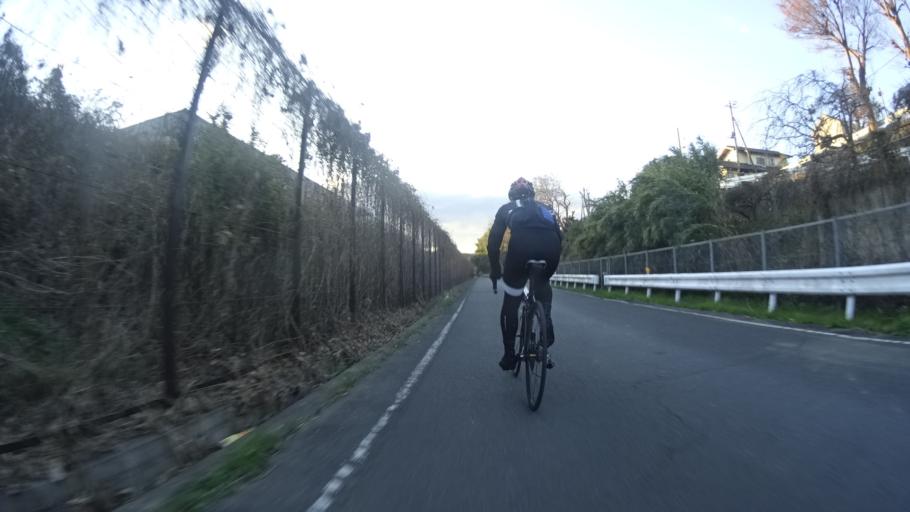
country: JP
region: Kanagawa
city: Zama
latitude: 35.4787
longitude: 139.3712
